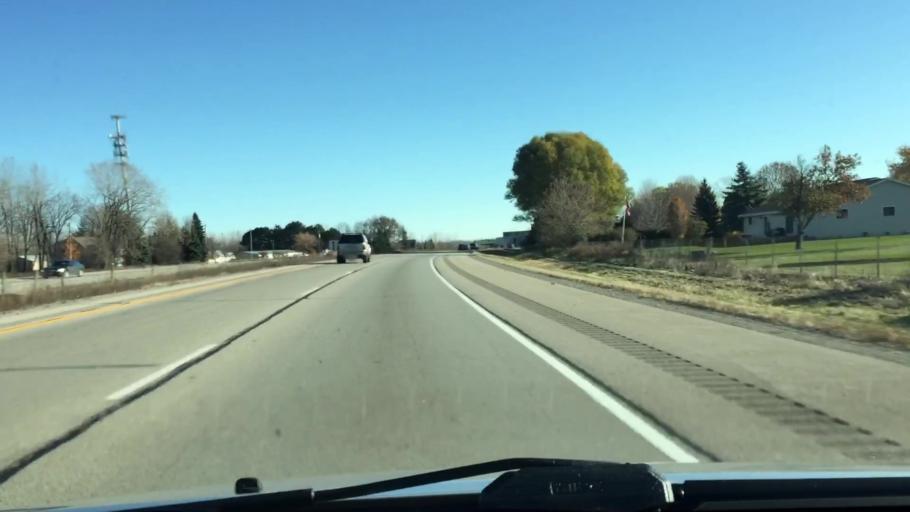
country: US
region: Wisconsin
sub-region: Outagamie County
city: Appleton
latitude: 44.2969
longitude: -88.4604
